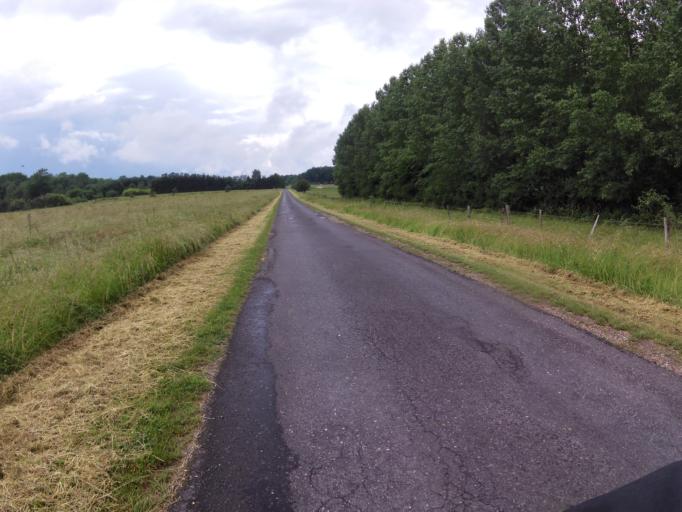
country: FR
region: Champagne-Ardenne
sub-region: Departement de la Marne
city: Sermaize-les-Bains
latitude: 48.7723
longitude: 4.9311
